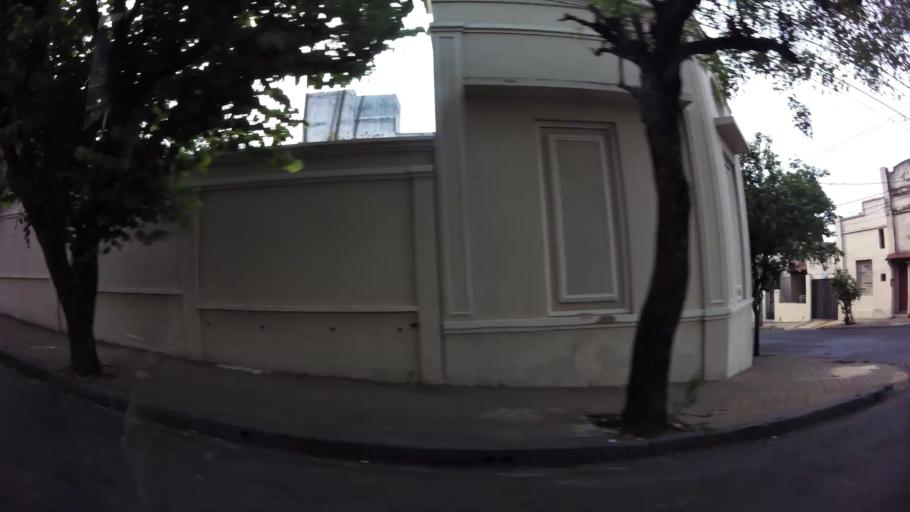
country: PY
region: Asuncion
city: Asuncion
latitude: -25.2935
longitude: -57.6181
